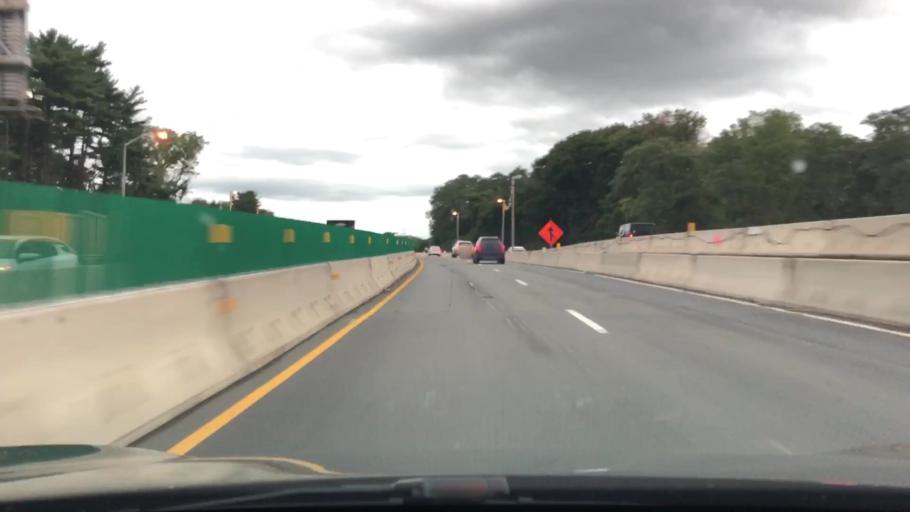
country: US
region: Pennsylvania
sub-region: Bucks County
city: Yardley
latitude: 40.2615
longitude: -74.8429
